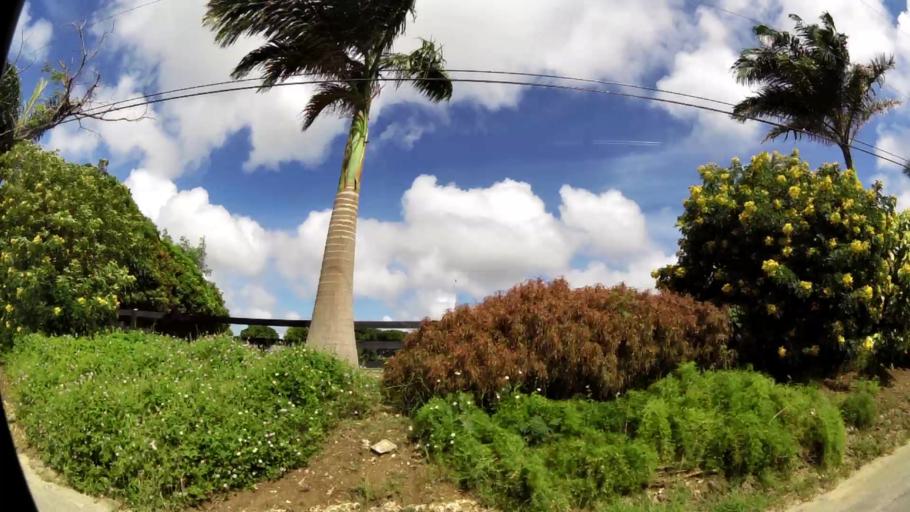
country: BB
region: Saint James
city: Holetown
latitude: 13.2154
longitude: -59.6110
